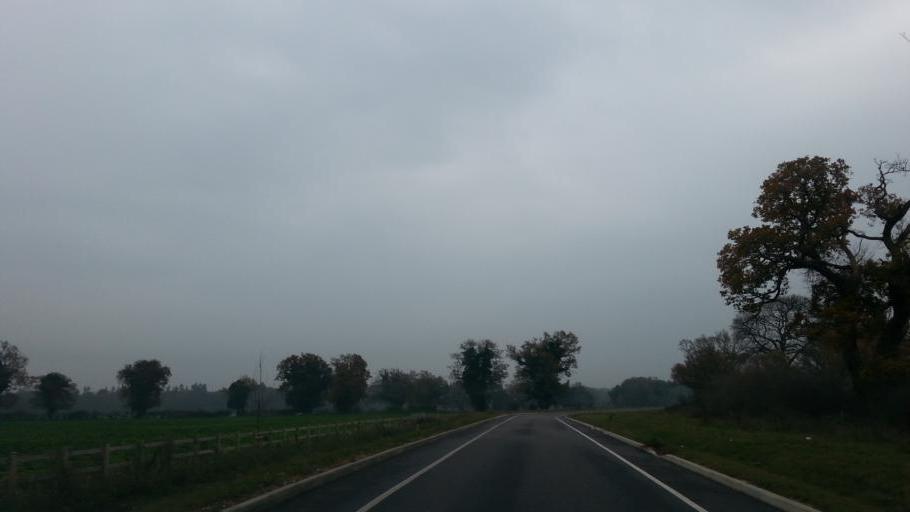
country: GB
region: England
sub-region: Suffolk
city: Thurston
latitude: 52.2433
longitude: 0.7812
